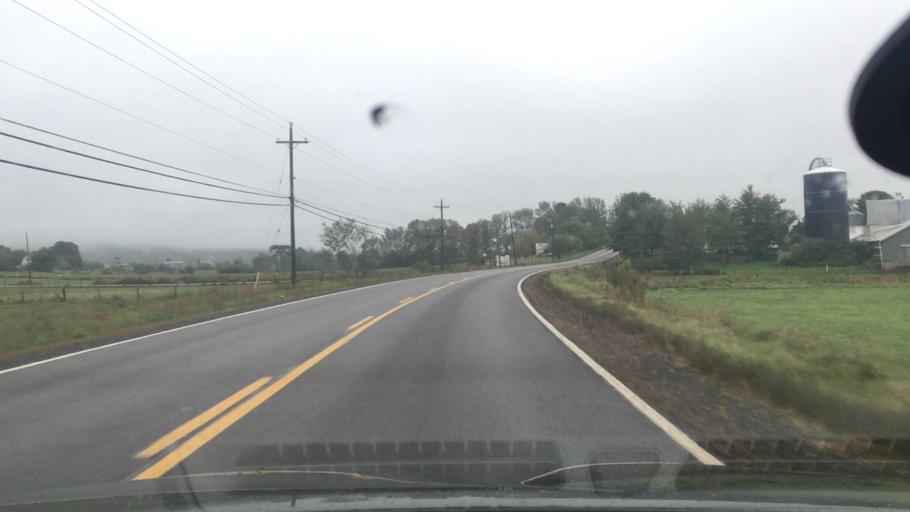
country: CA
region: Nova Scotia
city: Windsor
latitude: 44.9704
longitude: -64.1404
